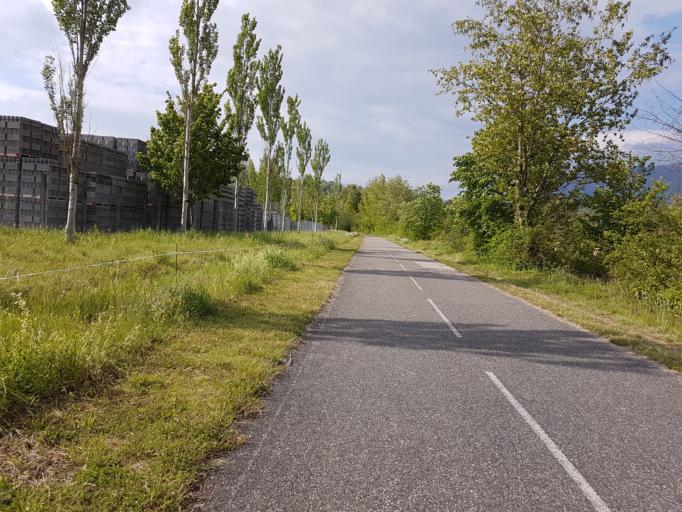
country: FR
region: Rhone-Alpes
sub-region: Departement de la Haute-Savoie
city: Versonnex
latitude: 45.9386
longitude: 5.8336
